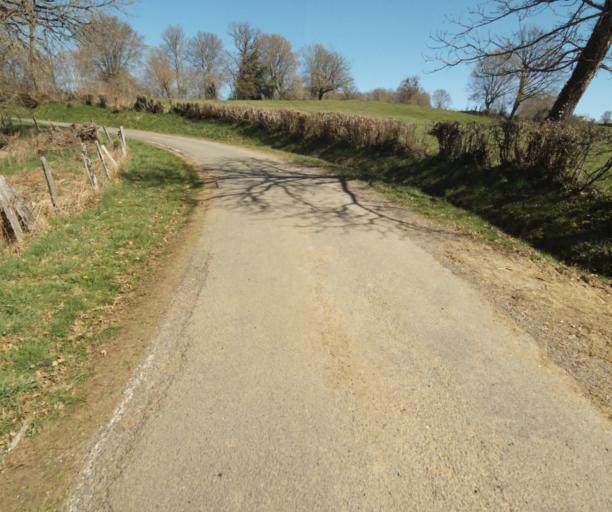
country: FR
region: Limousin
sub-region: Departement de la Correze
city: Uzerche
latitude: 45.4077
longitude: 1.6115
